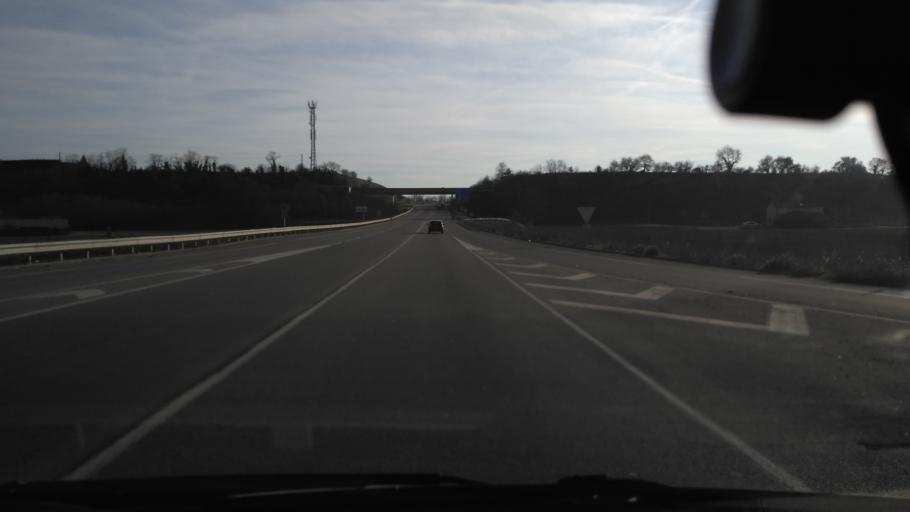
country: FR
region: Rhone-Alpes
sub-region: Departement de la Drome
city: Bourg-de-Peage
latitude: 45.0304
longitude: 5.0800
